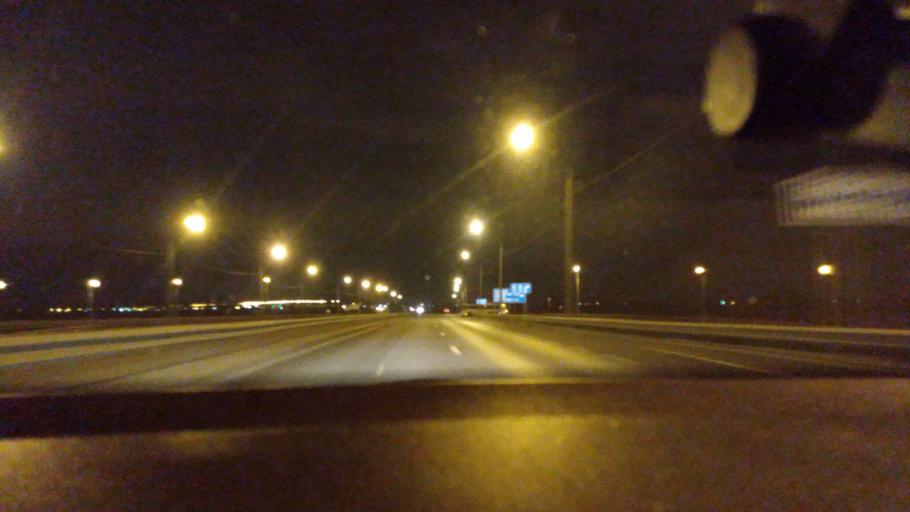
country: RU
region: Moskovskaya
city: Raduzhnyy
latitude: 55.1325
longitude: 38.7760
